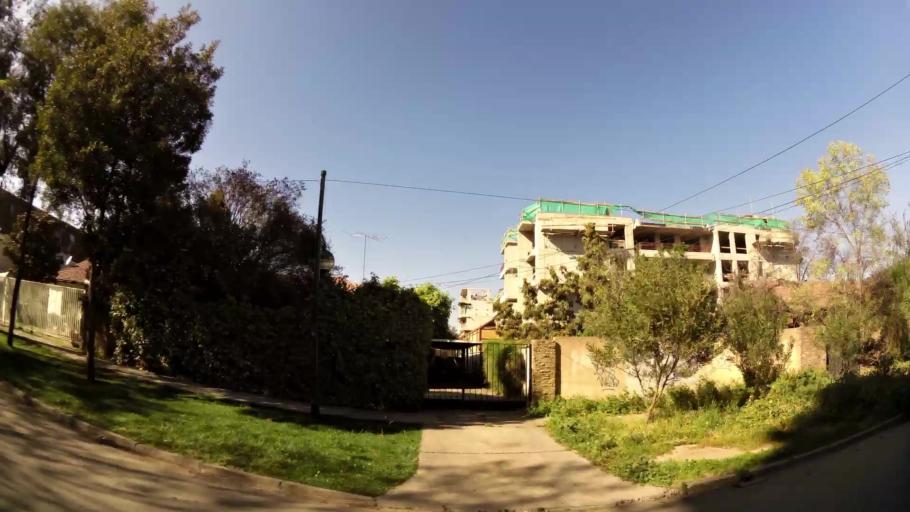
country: CL
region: Santiago Metropolitan
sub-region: Provincia de Santiago
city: Villa Presidente Frei, Nunoa, Santiago, Chile
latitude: -33.4446
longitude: -70.5783
